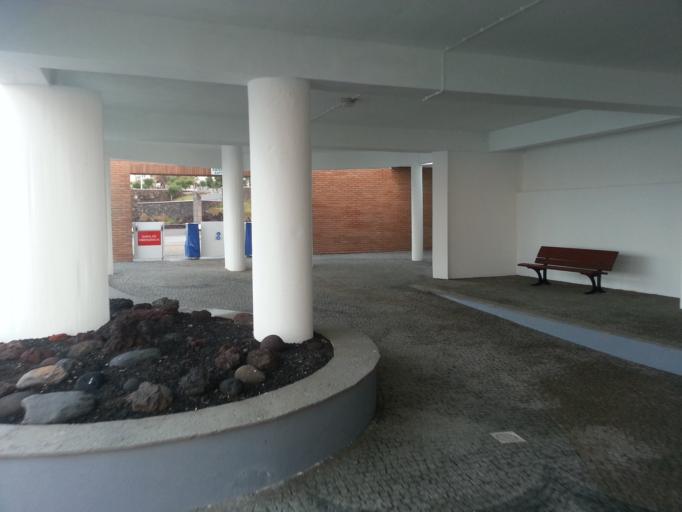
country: PT
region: Madeira
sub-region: Porto Moniz
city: Porto Moniz
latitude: 32.8683
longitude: -17.1704
